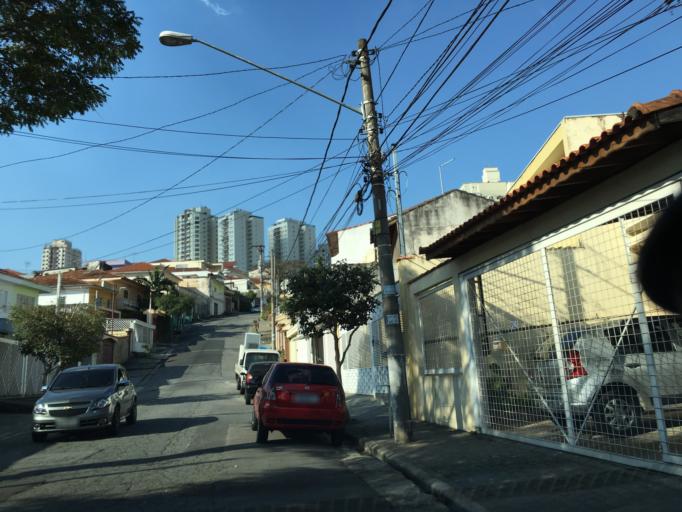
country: BR
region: Sao Paulo
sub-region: Sao Paulo
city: Sao Paulo
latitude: -23.4733
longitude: -46.6340
